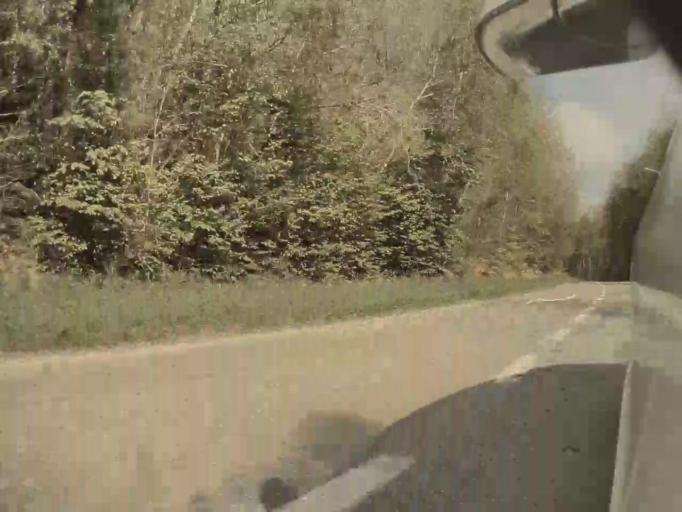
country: BE
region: Wallonia
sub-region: Province du Luxembourg
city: Tellin
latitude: 50.0545
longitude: 5.2105
